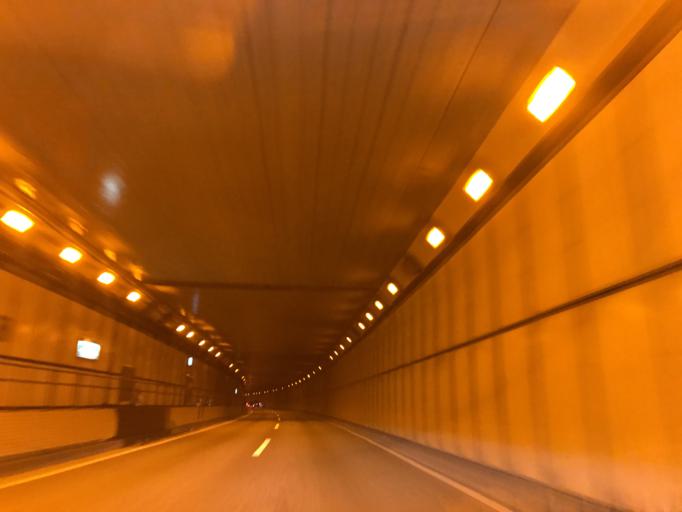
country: JP
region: Tokyo
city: Tokyo
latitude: 35.6887
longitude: 139.7075
